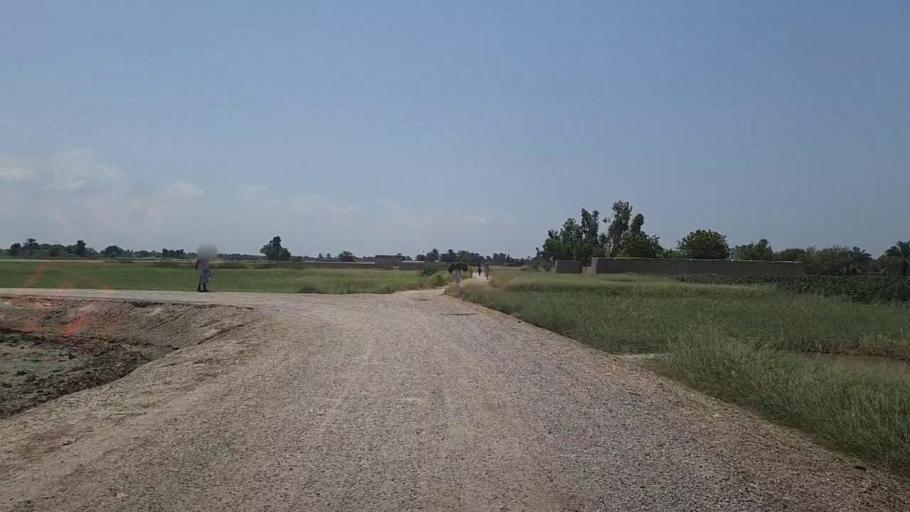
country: PK
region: Sindh
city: Ubauro
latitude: 28.1642
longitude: 69.7634
